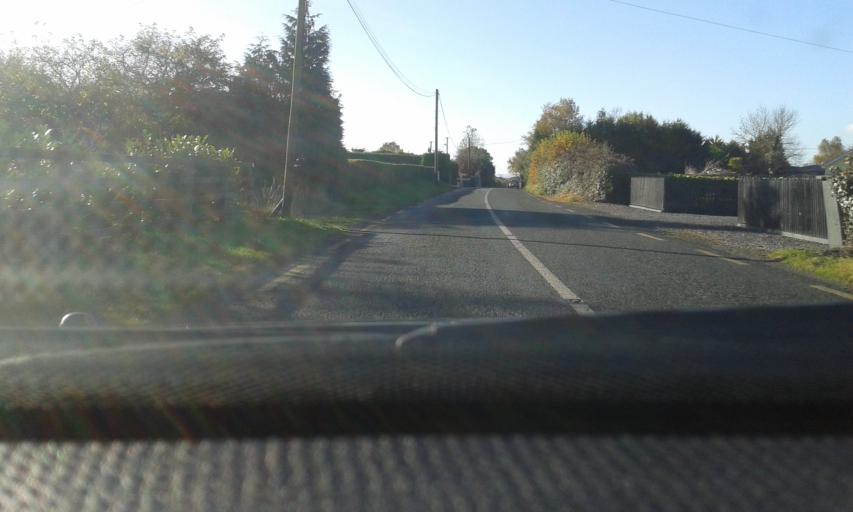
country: IE
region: Leinster
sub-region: Kildare
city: Monasterevin
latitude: 53.1730
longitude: -7.0271
